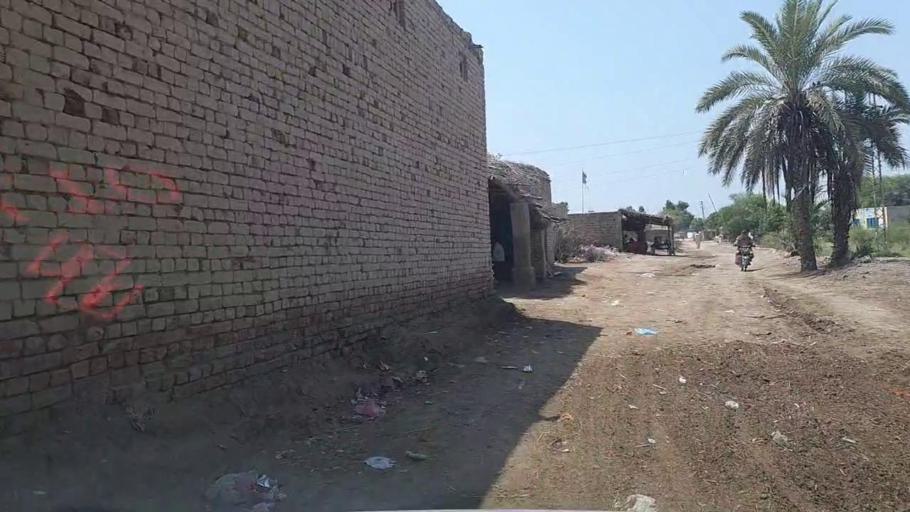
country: PK
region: Sindh
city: Ubauro
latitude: 28.1951
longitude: 69.8009
